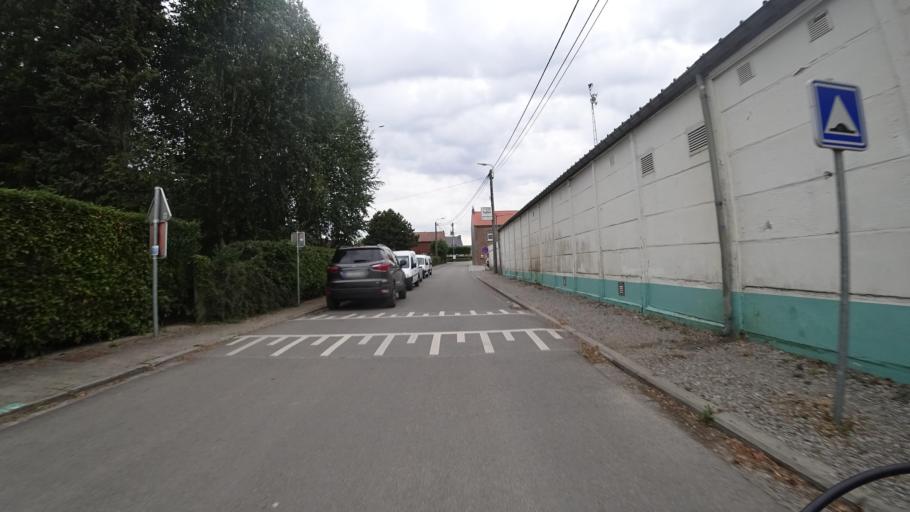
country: BE
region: Wallonia
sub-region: Province du Brabant Wallon
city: Perwez
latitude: 50.5532
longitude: 4.7952
